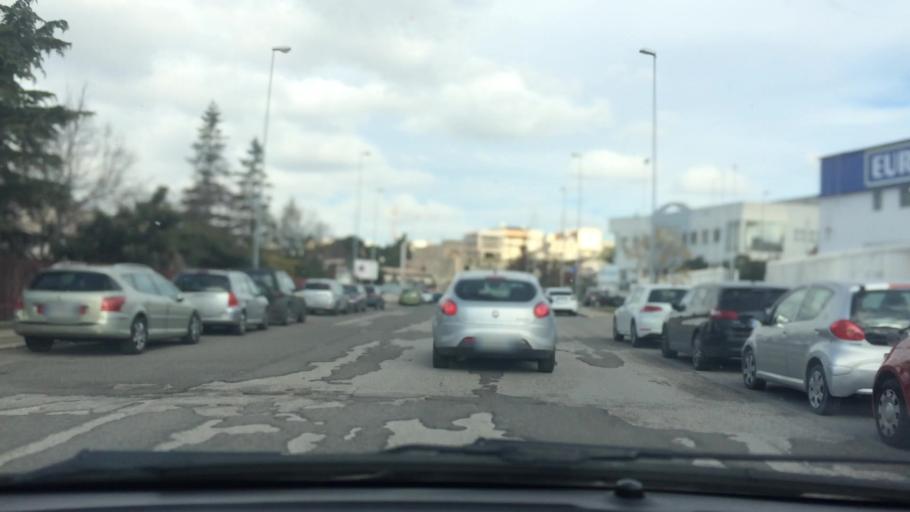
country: IT
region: Basilicate
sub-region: Provincia di Matera
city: Matera
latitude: 40.6726
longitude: 16.5733
